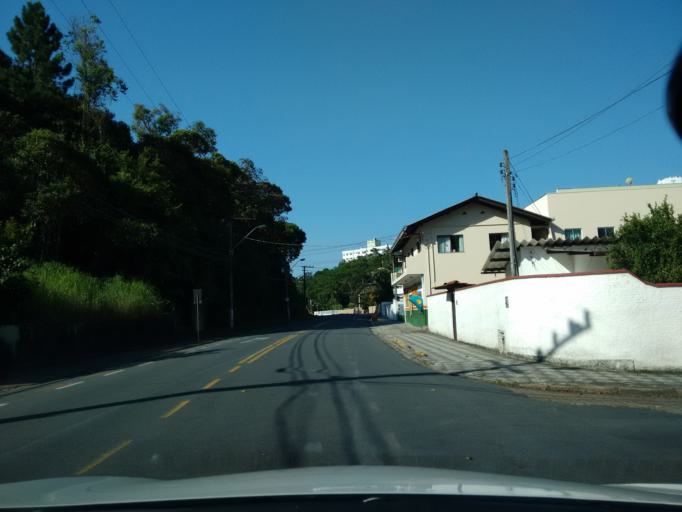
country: BR
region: Santa Catarina
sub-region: Blumenau
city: Blumenau
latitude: -26.8999
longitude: -49.0662
